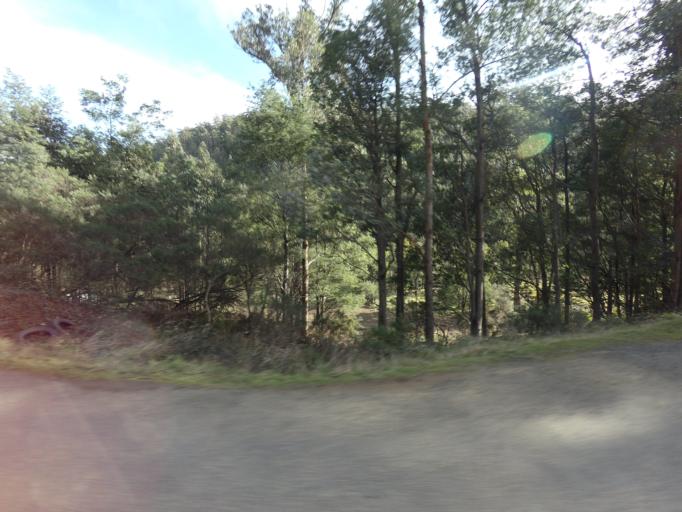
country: AU
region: Tasmania
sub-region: Huon Valley
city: Huonville
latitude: -43.0379
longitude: 147.1387
